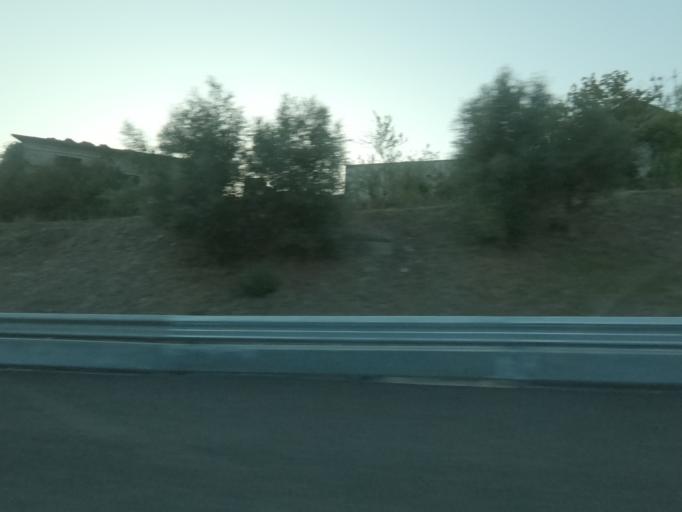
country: PT
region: Leiria
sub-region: Leiria
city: Leiria
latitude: 39.7430
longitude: -8.7915
